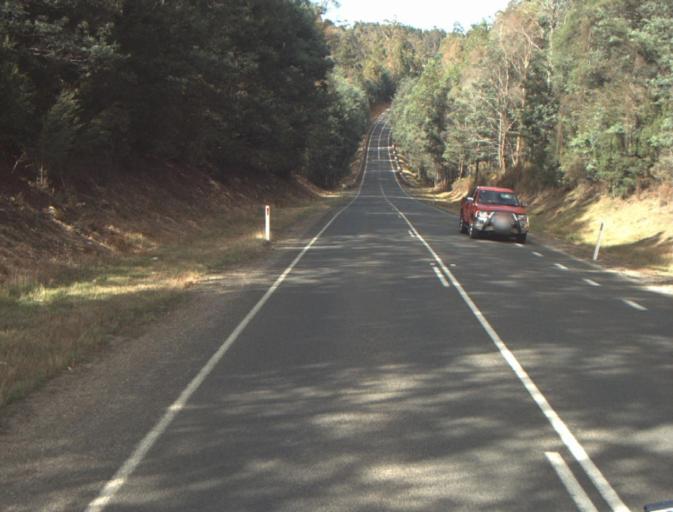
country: AU
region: Tasmania
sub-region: Launceston
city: Mayfield
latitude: -41.2935
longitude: 147.2150
